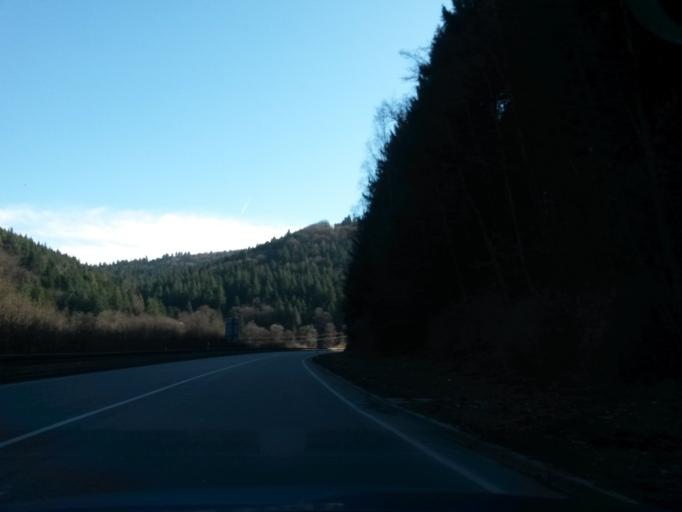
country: DE
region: Baden-Wuerttemberg
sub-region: Karlsruhe Region
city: Birkenfeld
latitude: 48.8610
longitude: 8.6380
